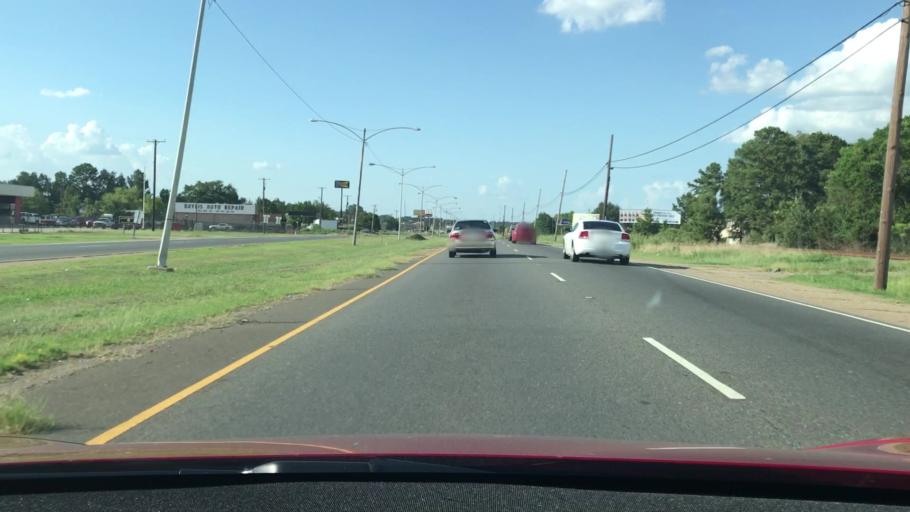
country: US
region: Louisiana
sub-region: Bossier Parish
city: Bossier City
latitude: 32.4360
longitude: -93.7827
